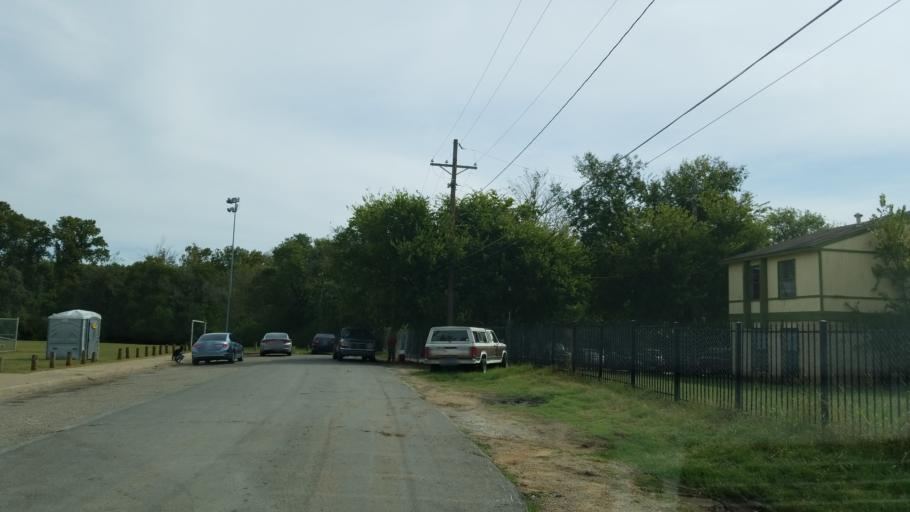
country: US
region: Texas
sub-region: Dallas County
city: Dallas
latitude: 32.7608
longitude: -96.7369
